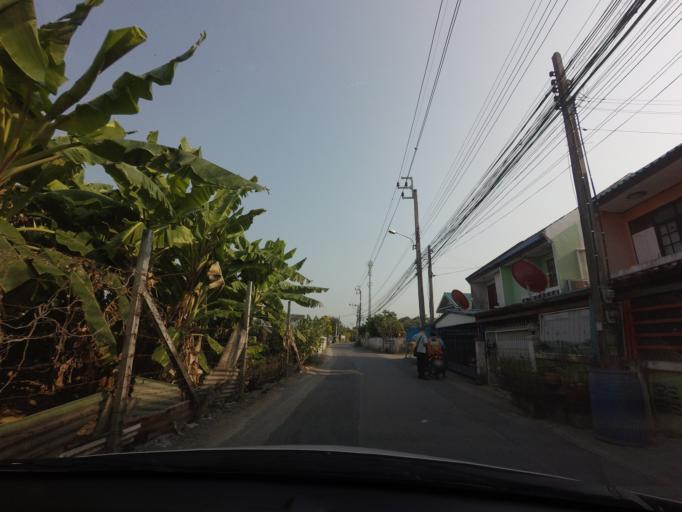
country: TH
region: Nonthaburi
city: Bang Yai
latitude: 13.8078
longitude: 100.3725
